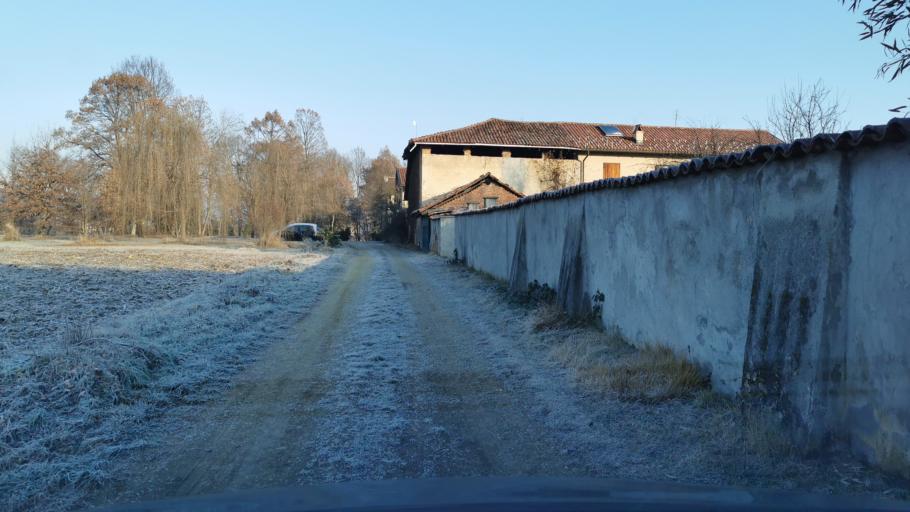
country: IT
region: Piedmont
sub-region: Provincia di Torino
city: Rivarossa
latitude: 45.2458
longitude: 7.7173
